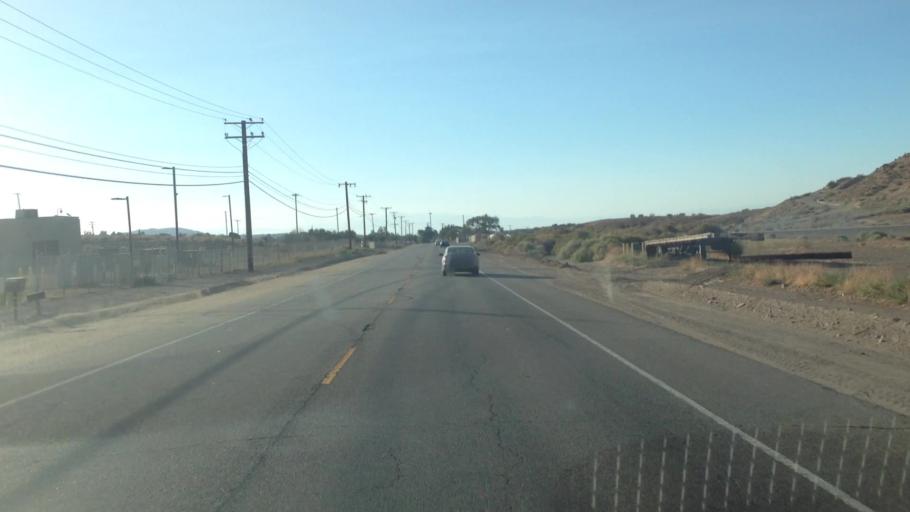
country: US
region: California
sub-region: Los Angeles County
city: Vincent
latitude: 34.5340
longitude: -118.1026
